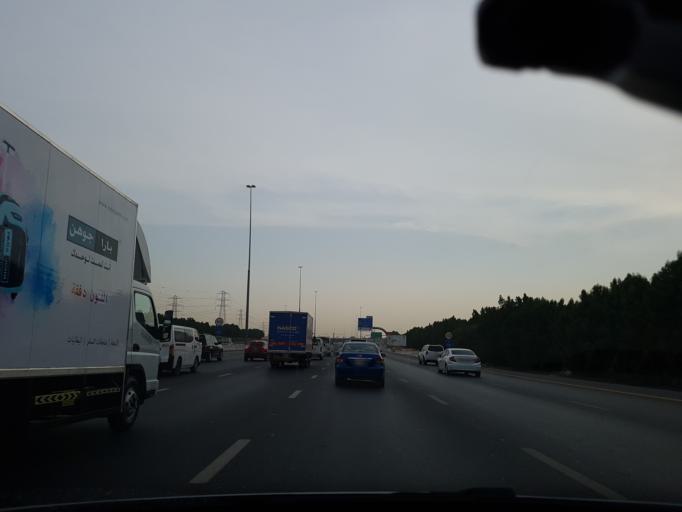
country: AE
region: Ash Shariqah
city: Sharjah
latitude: 25.2592
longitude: 55.4076
